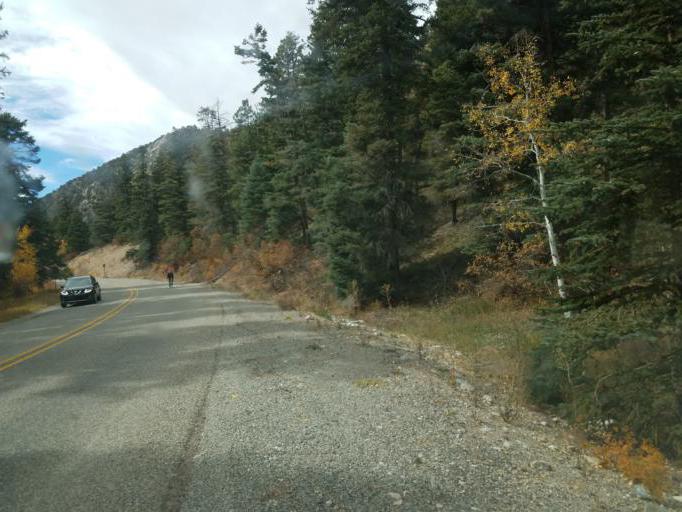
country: US
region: New Mexico
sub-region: Taos County
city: Arroyo Seco
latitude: 36.5512
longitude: -105.5429
